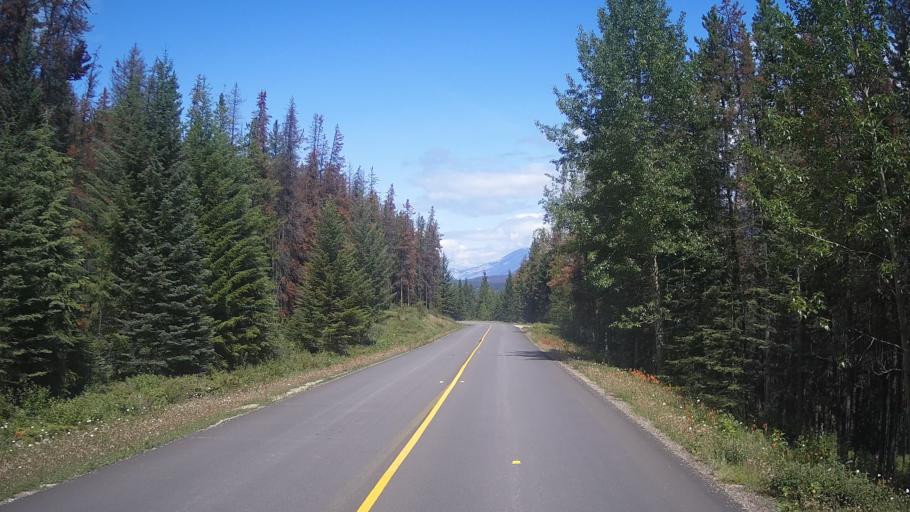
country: CA
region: Alberta
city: Jasper Park Lodge
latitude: 52.7840
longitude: -118.0326
